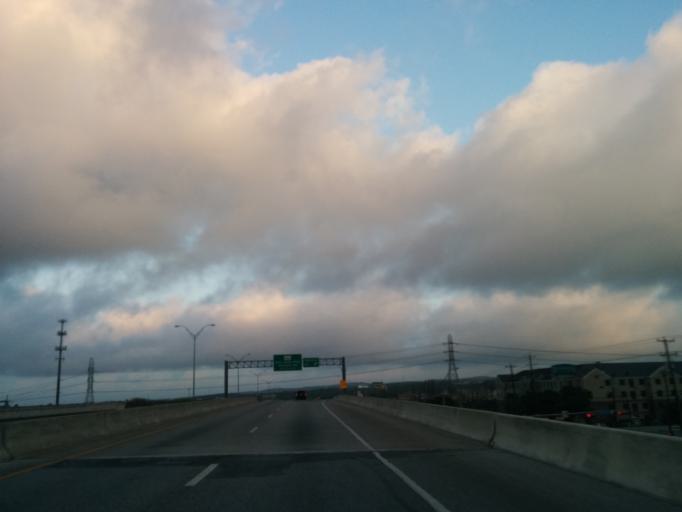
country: US
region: Texas
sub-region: Bexar County
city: Helotes
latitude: 29.5882
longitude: -98.6233
